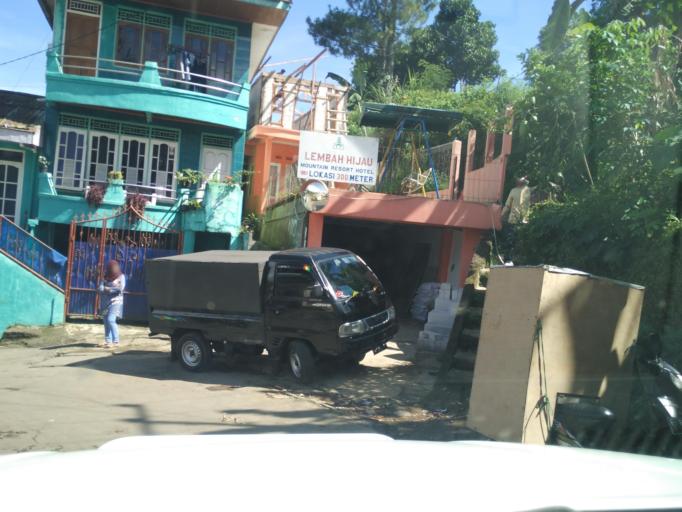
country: ID
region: West Java
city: Caringin
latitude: -6.7159
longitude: 107.0099
